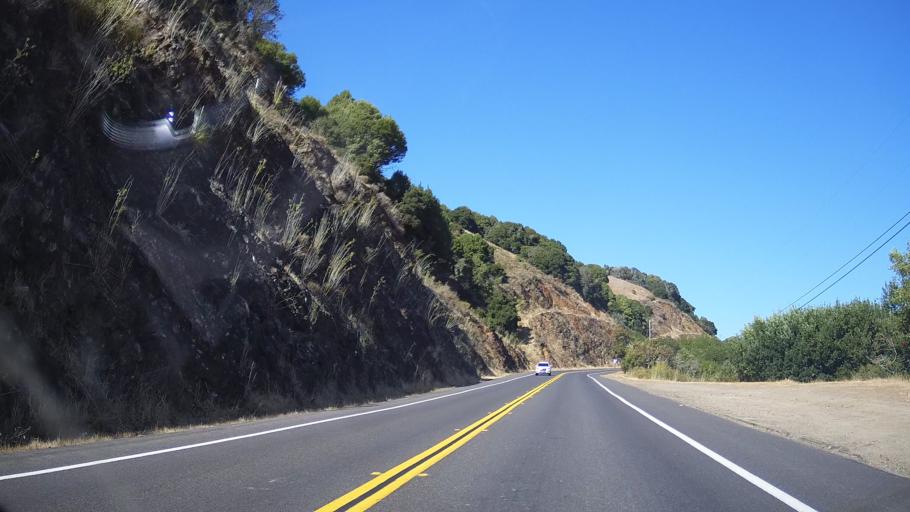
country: US
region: California
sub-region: Marin County
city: Lagunitas-Forest Knolls
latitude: 38.0740
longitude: -122.7572
